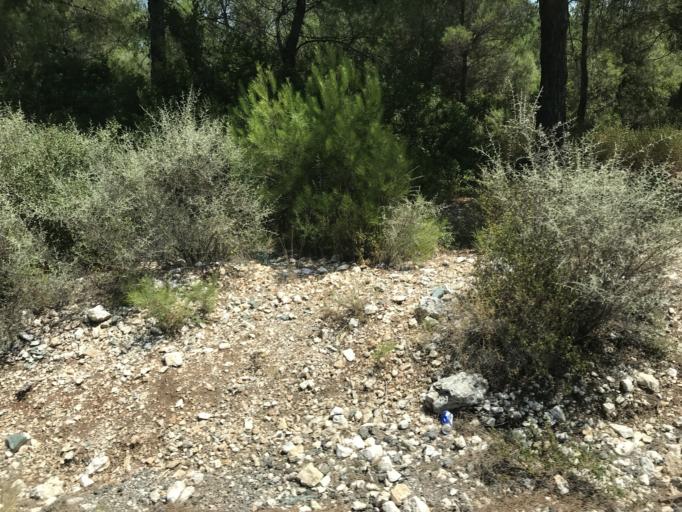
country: TR
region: Izmir
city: Urla
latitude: 38.2624
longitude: 26.7368
